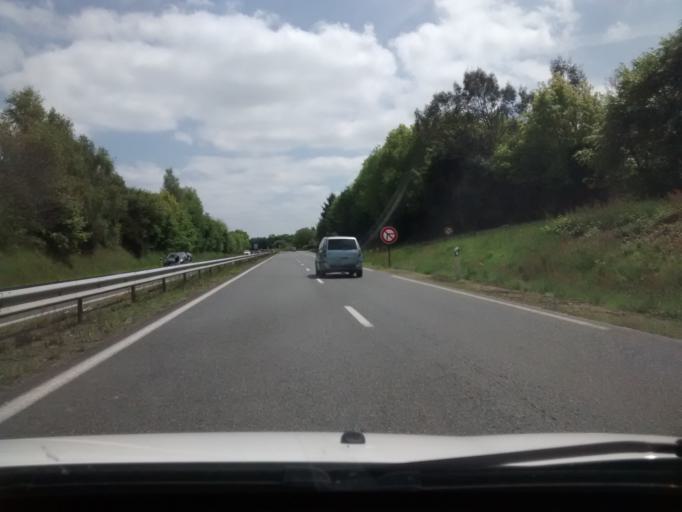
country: FR
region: Brittany
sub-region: Departement des Cotes-d'Armor
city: Cavan
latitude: 48.6576
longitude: -3.3370
